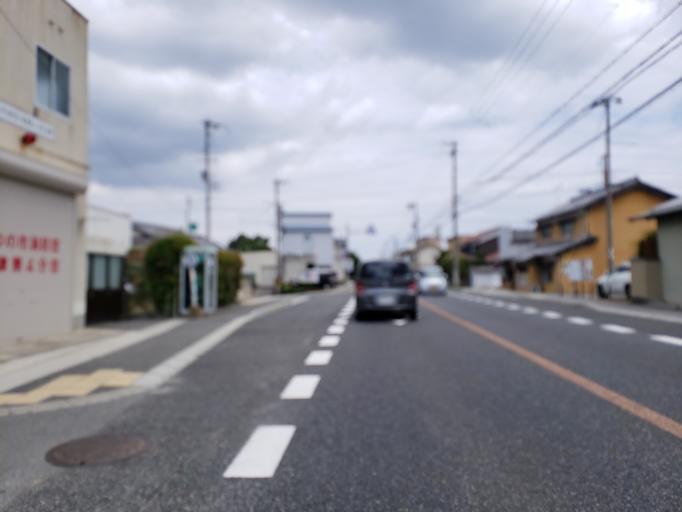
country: JP
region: Hyogo
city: Tatsunocho-tominaga
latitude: 34.7832
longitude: 134.5581
